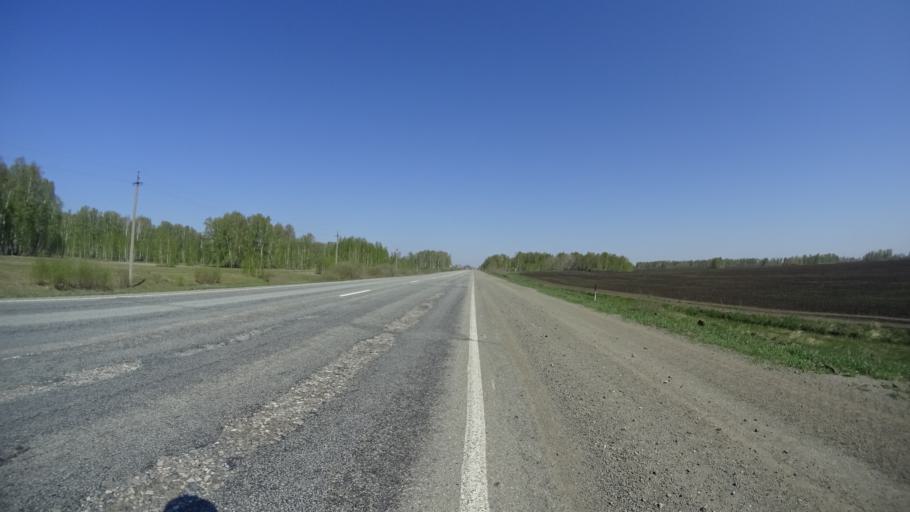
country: RU
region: Chelyabinsk
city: Troitsk
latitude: 54.1799
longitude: 61.4350
